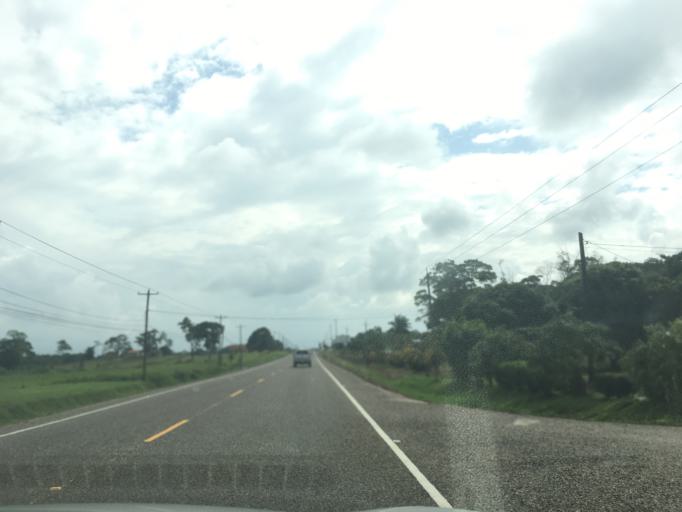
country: BZ
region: Stann Creek
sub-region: Dangriga
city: Dangriga
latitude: 16.9890
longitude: -88.2986
